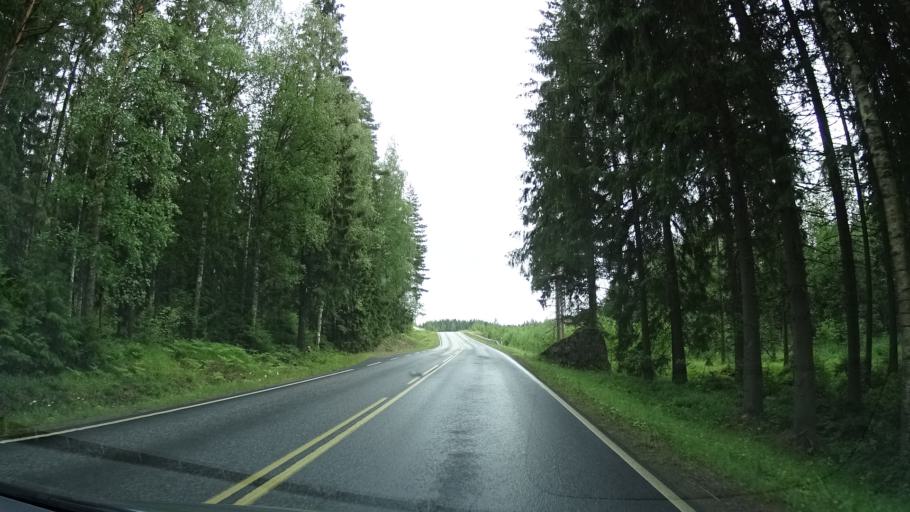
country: FI
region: Haeme
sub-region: Forssa
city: Humppila
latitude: 61.0972
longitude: 23.3464
